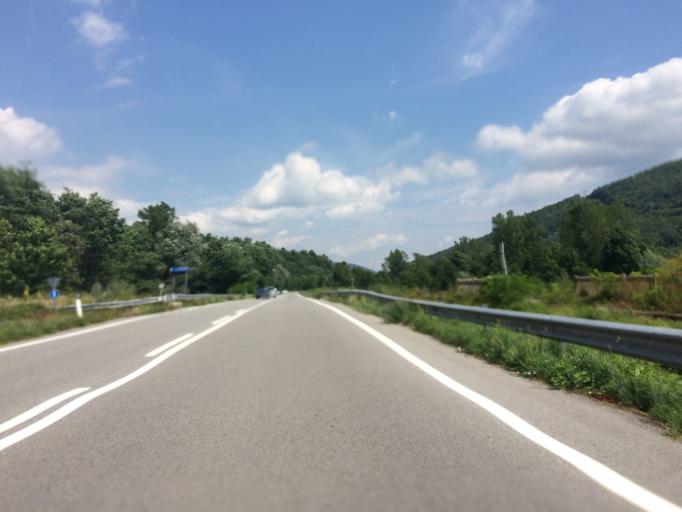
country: IT
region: Piedmont
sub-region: Provincia di Cuneo
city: Garessio
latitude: 44.2219
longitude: 8.0151
